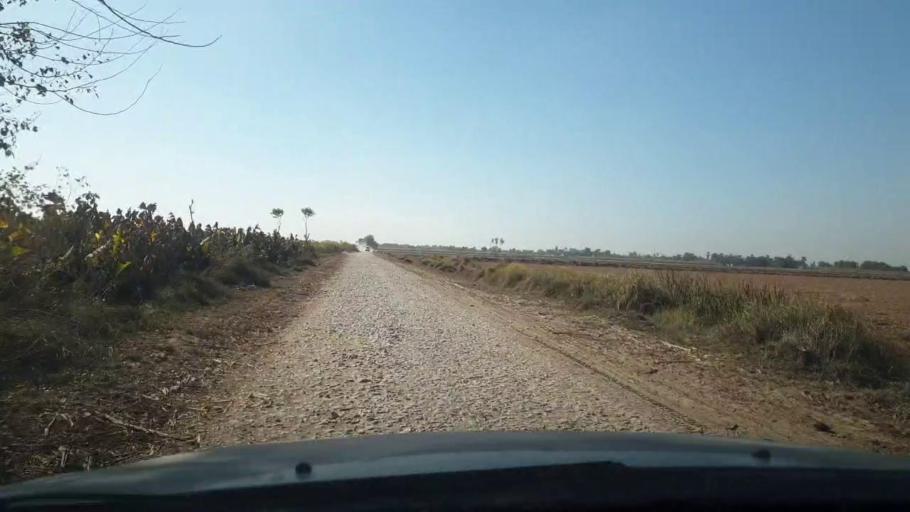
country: PK
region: Sindh
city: Ghotki
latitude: 27.9840
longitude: 69.2182
